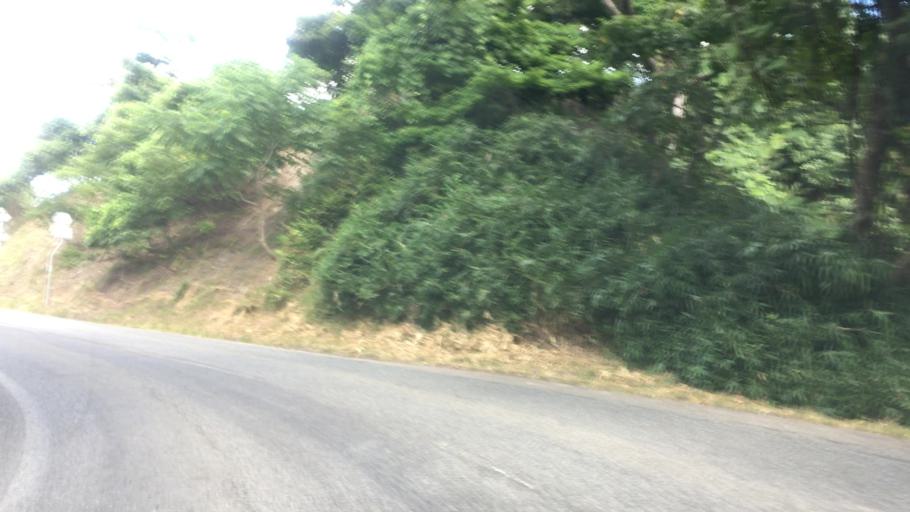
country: JP
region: Hyogo
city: Toyooka
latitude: 35.5144
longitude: 134.7831
